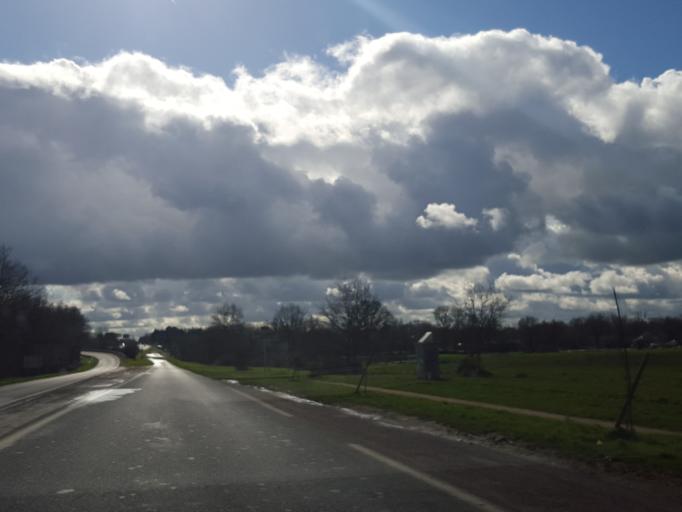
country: FR
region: Pays de la Loire
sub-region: Departement de la Vendee
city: Belleville-sur-Vie
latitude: 46.7740
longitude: -1.4308
